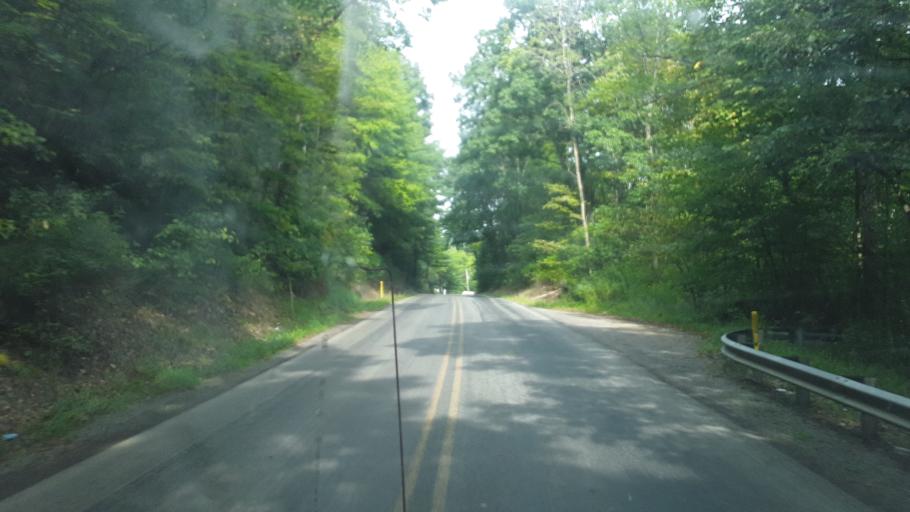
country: US
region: Pennsylvania
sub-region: Jefferson County
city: Punxsutawney
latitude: 40.9076
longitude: -79.0432
